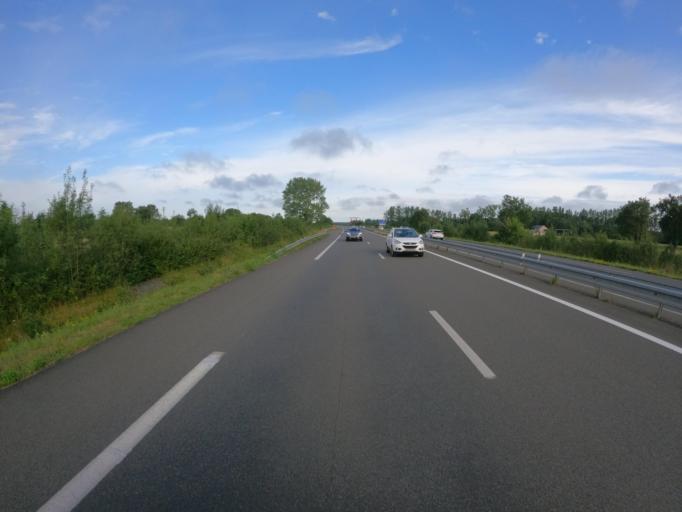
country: FR
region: Pays de la Loire
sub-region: Departement de Maine-et-Loire
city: Allonnes
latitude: 47.2841
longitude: 0.0159
